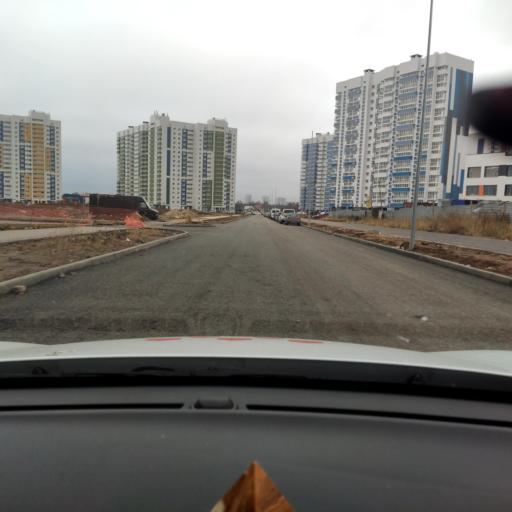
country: RU
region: Tatarstan
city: Osinovo
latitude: 55.8573
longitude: 48.9024
